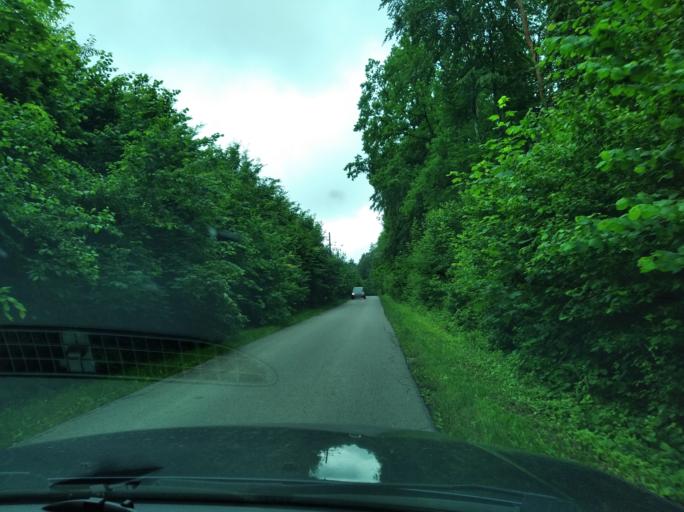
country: PL
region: Subcarpathian Voivodeship
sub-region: Powiat jaroslawski
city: Pruchnik
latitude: 49.8925
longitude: 22.5262
